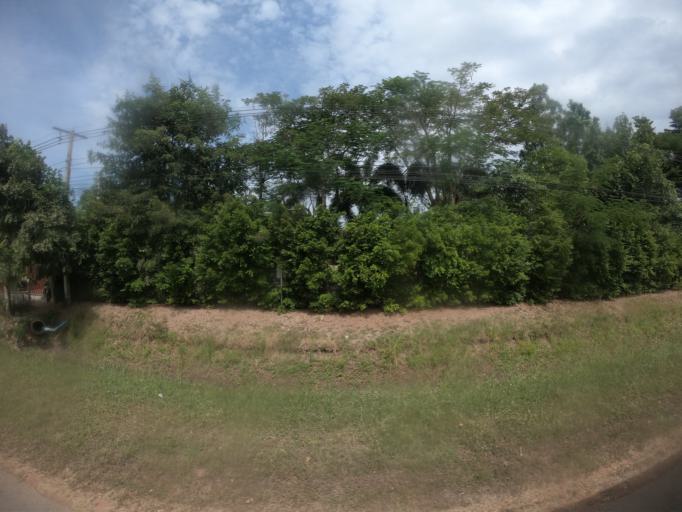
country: TH
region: Maha Sarakham
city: Chiang Yuen
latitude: 16.3434
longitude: 103.1368
